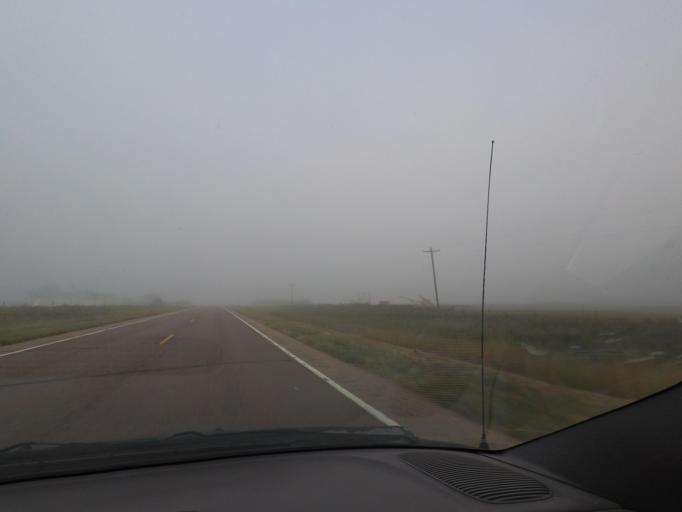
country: US
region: Colorado
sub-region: Kit Carson County
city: Burlington
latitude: 39.6577
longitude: -102.5630
